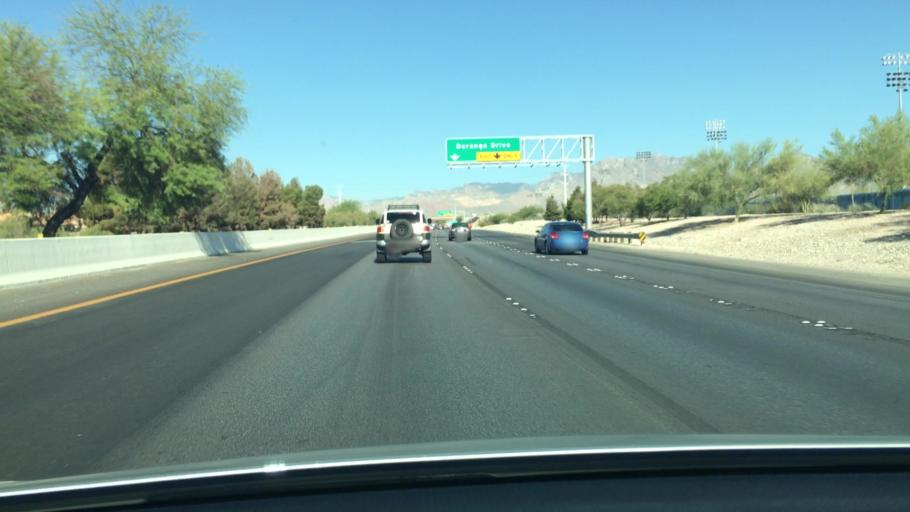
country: US
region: Nevada
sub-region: Clark County
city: Spring Valley
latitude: 36.1782
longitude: -115.2662
